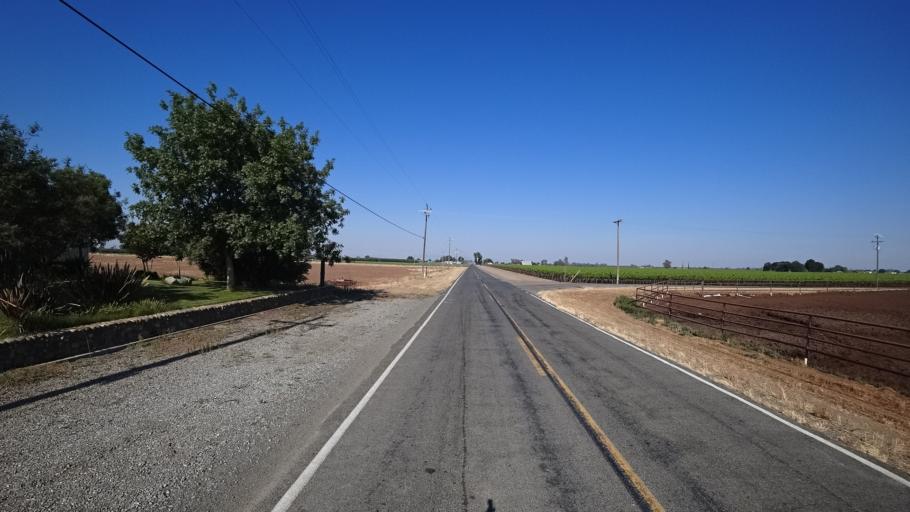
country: US
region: California
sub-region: Fresno County
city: Riverdale
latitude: 36.3657
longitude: -119.8426
